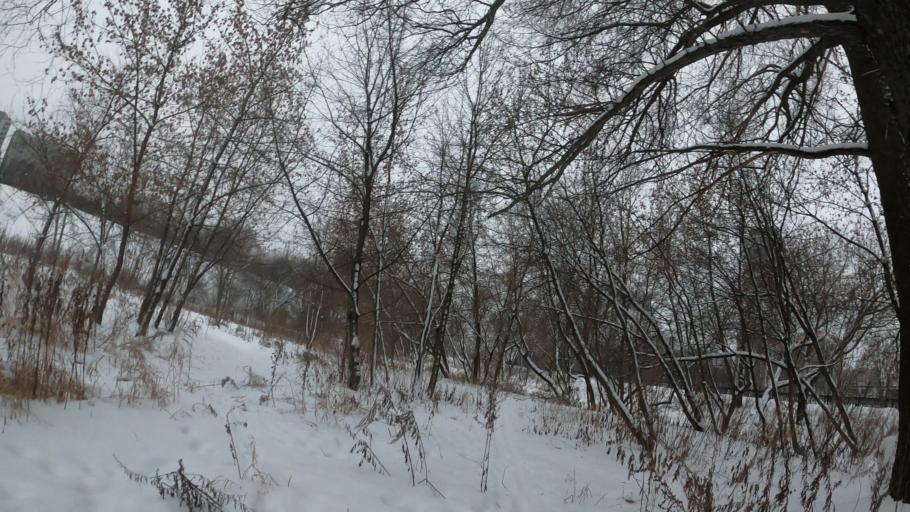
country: RU
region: Moskovskaya
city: Levoberezhnaya
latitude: 55.8995
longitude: 37.4705
